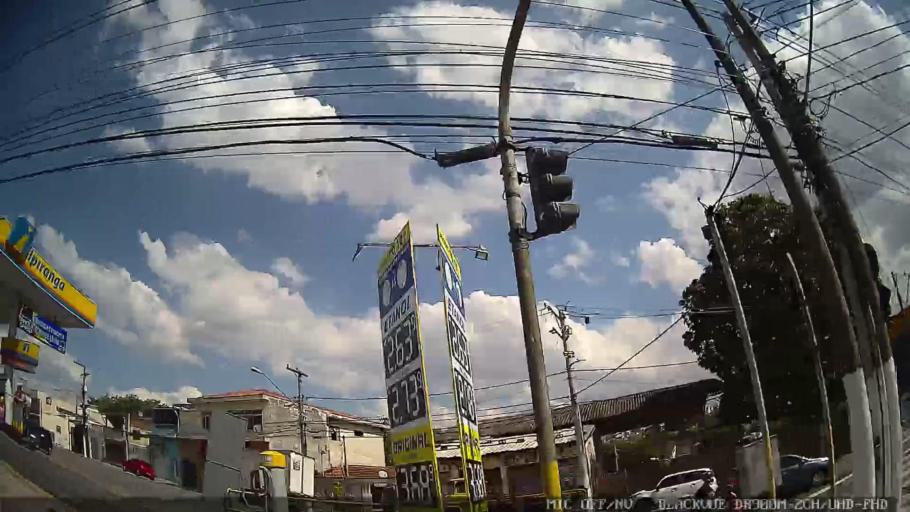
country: BR
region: Sao Paulo
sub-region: Guarulhos
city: Guarulhos
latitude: -23.5185
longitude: -46.5113
